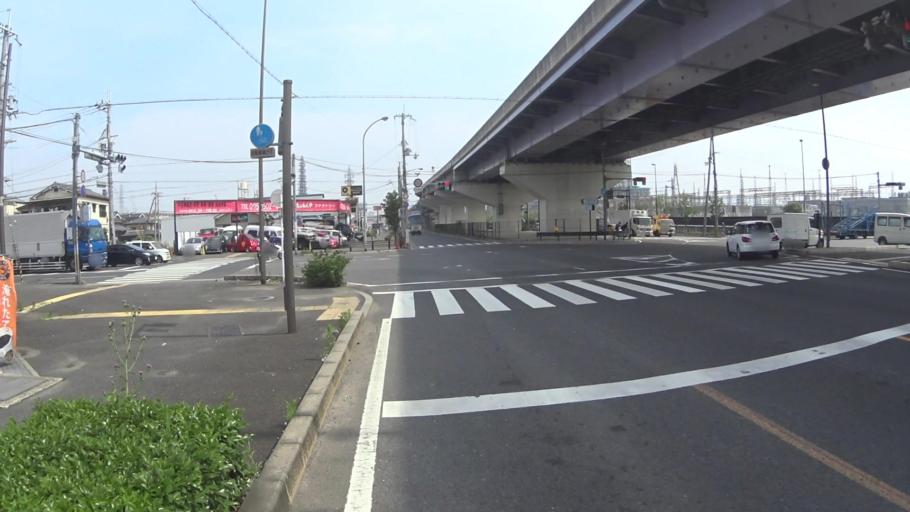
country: JP
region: Kyoto
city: Yawata
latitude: 34.8334
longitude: 135.7223
